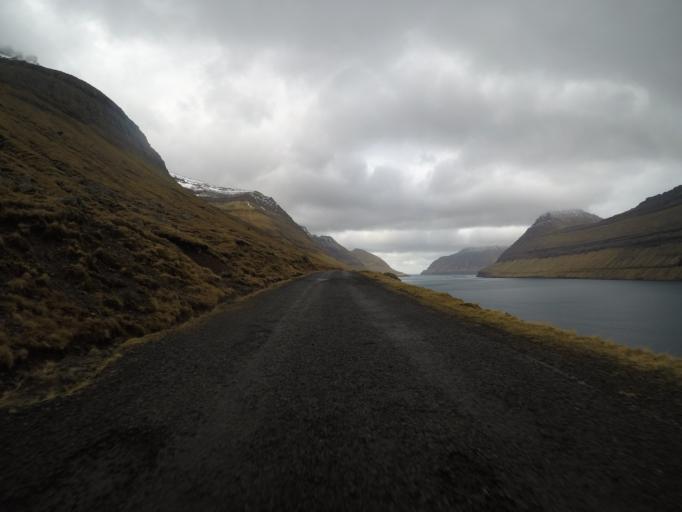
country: FO
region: Nordoyar
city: Klaksvik
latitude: 62.3116
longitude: -6.5488
